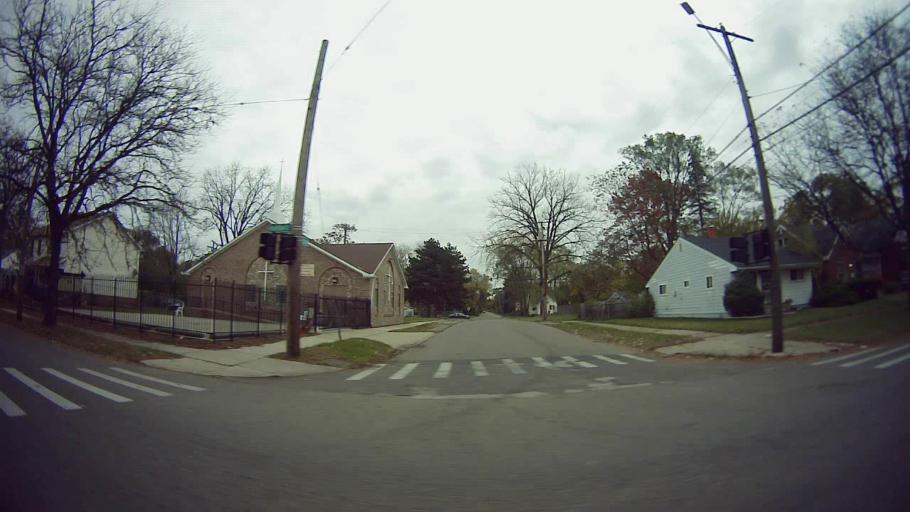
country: US
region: Michigan
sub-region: Oakland County
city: Oak Park
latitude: 42.4054
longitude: -83.1891
